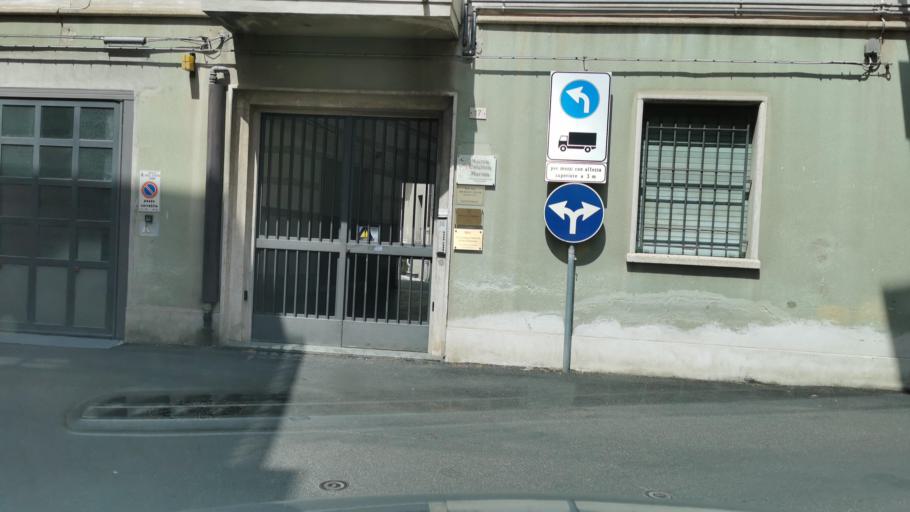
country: IT
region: Emilia-Romagna
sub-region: Provincia di Bologna
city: Castel San Pietro Terme
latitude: 44.3980
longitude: 11.5909
